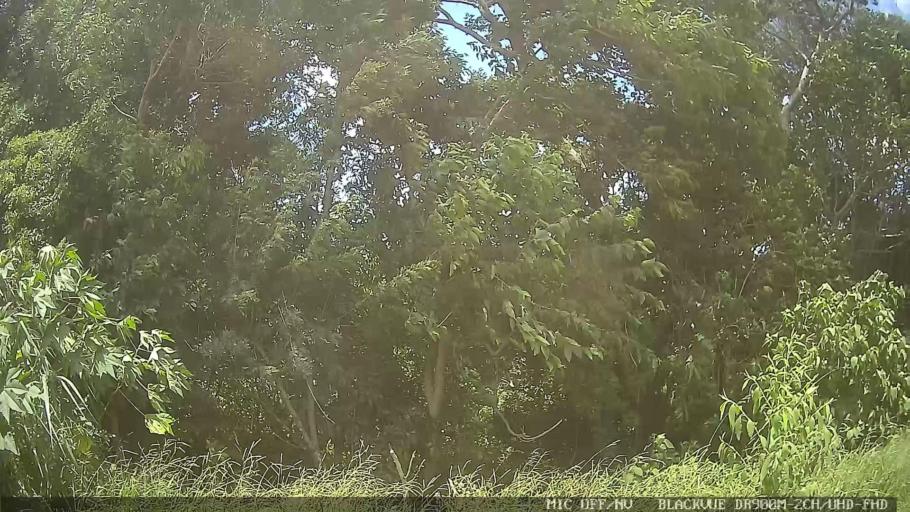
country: BR
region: Sao Paulo
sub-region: Braganca Paulista
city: Braganca Paulista
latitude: -23.0239
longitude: -46.5473
